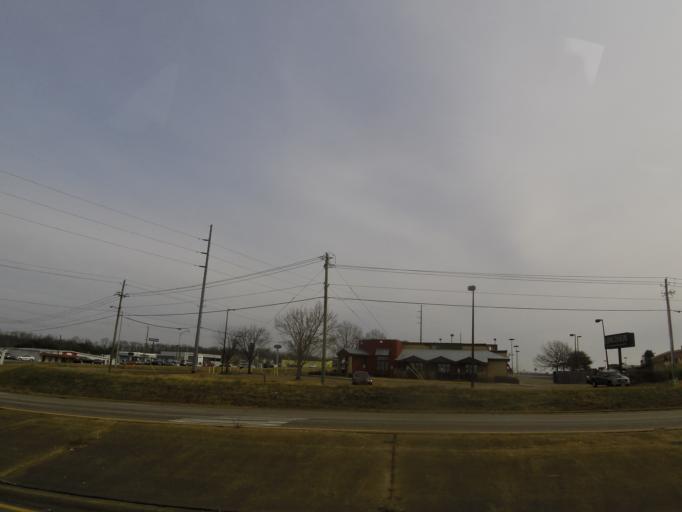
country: US
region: Alabama
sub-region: Montgomery County
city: Montgomery
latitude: 32.3263
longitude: -86.2412
